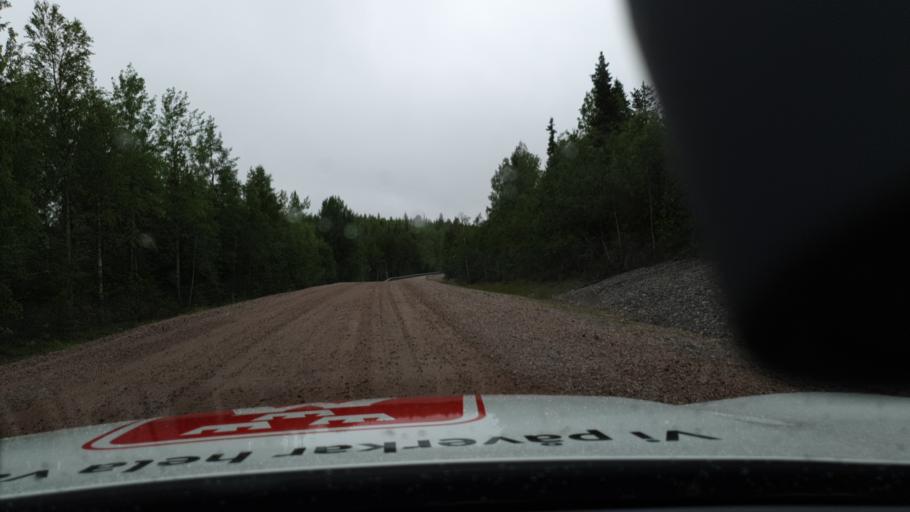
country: SE
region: Norrbotten
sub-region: Overtornea Kommun
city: OEvertornea
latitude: 66.5074
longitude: 23.4107
